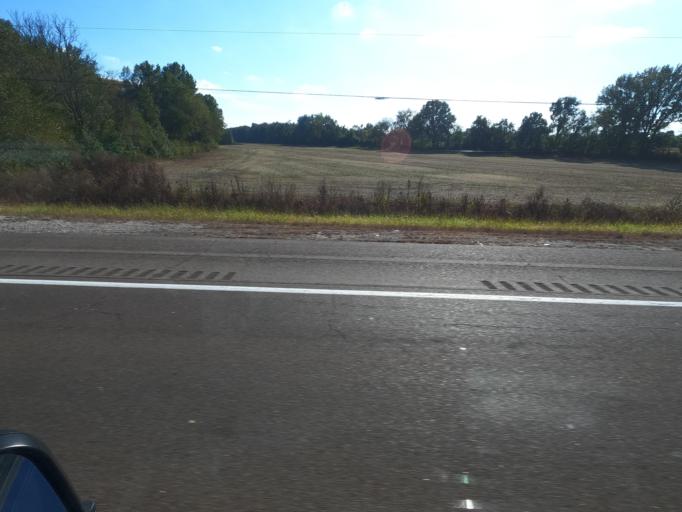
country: US
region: Tennessee
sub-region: Crockett County
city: Bells
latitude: 35.6912
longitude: -88.9976
